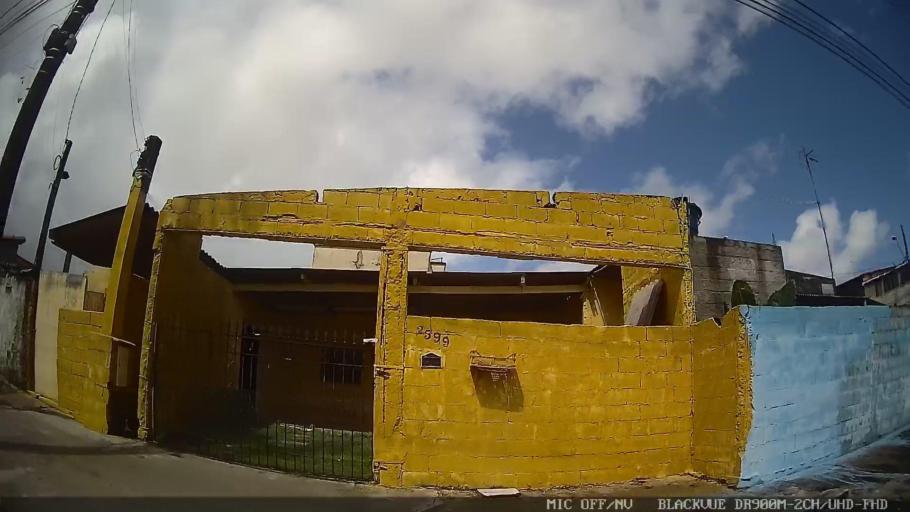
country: BR
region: Sao Paulo
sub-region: Itanhaem
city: Itanhaem
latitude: -24.1827
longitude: -46.8210
